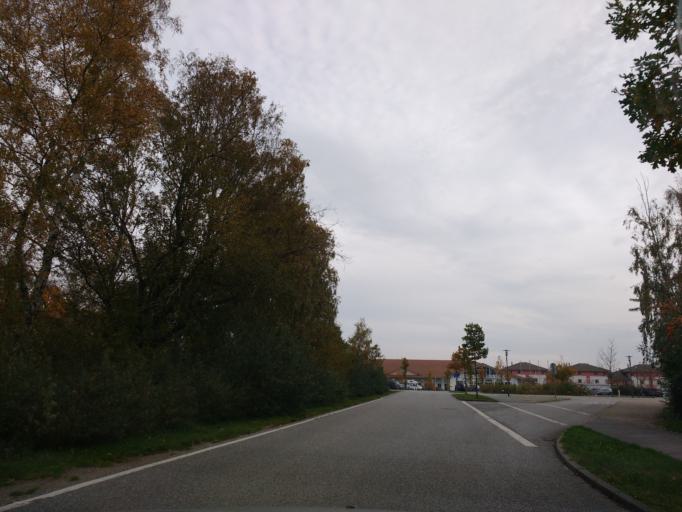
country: DE
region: Mecklenburg-Vorpommern
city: Ostseebad Boltenhagen
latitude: 53.9759
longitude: 11.2510
